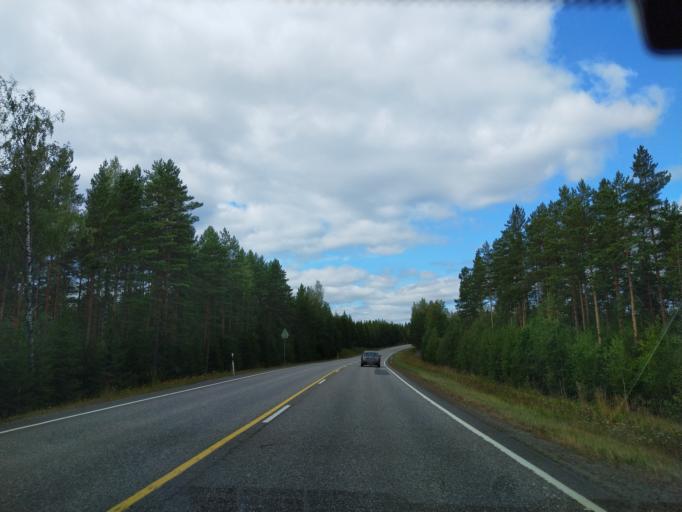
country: FI
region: Haeme
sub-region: Riihimaeki
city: Loppi
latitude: 60.7442
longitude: 24.3519
